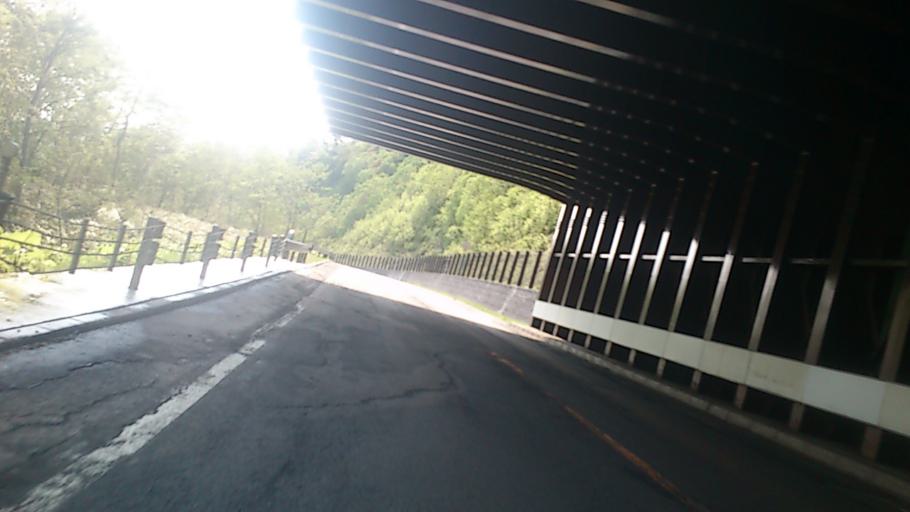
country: JP
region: Hokkaido
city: Bihoro
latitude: 43.4603
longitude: 144.2371
